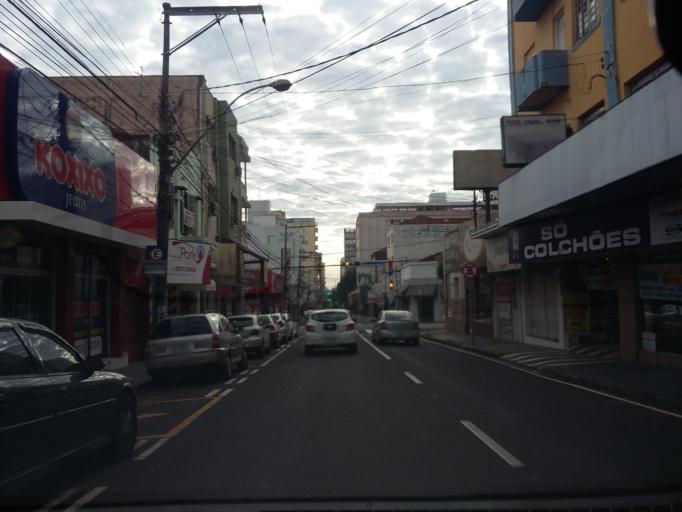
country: BR
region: Sao Paulo
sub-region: Sao Jose Do Rio Preto
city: Sao Jose do Rio Preto
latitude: -20.8149
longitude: -49.3844
